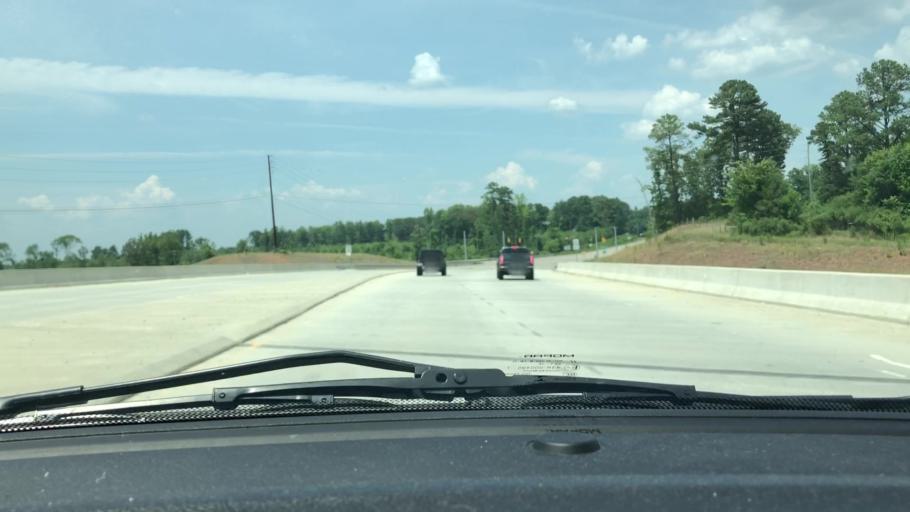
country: US
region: North Carolina
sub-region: Chatham County
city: Farmville
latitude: 35.5402
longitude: -79.2406
